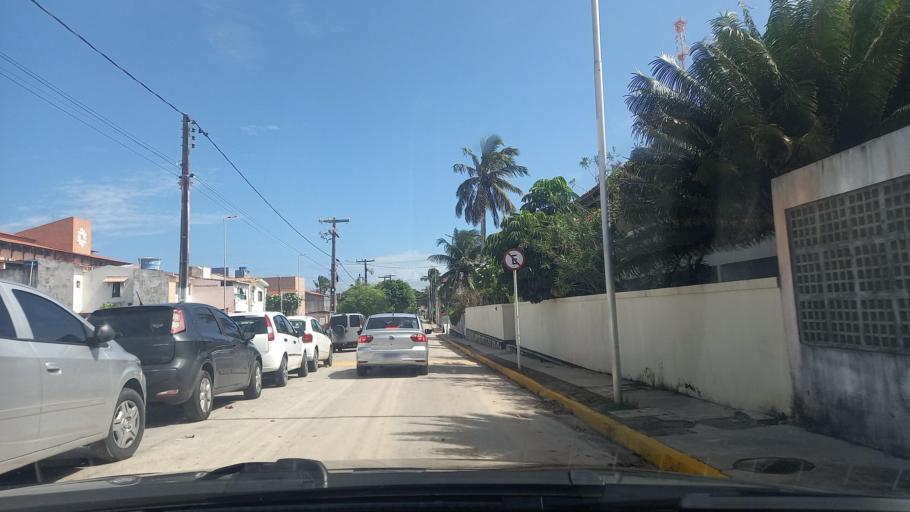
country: BR
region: Alagoas
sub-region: Marechal Deodoro
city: Marechal Deodoro
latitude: -9.7677
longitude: -35.8391
